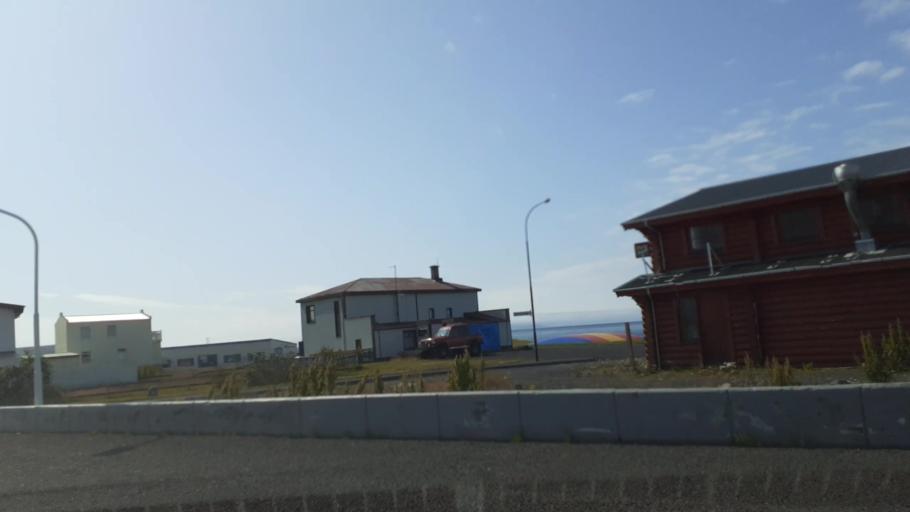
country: IS
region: Northwest
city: Saudarkrokur
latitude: 65.8237
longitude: -20.3064
